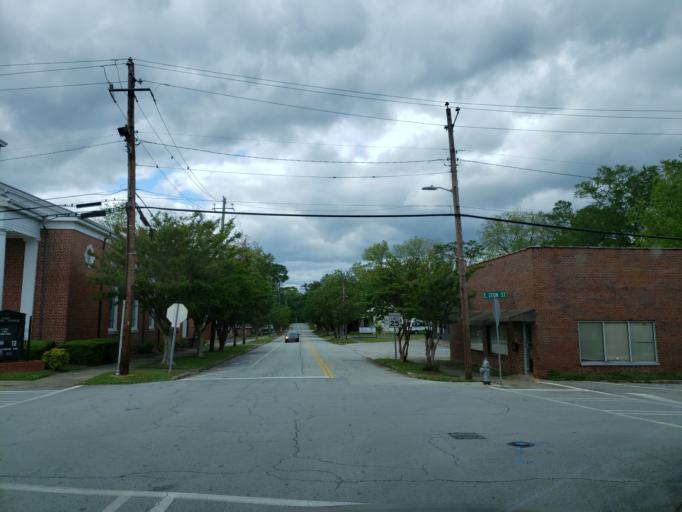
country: US
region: Georgia
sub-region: Haralson County
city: Tallapoosa
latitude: 33.7453
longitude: -85.2881
